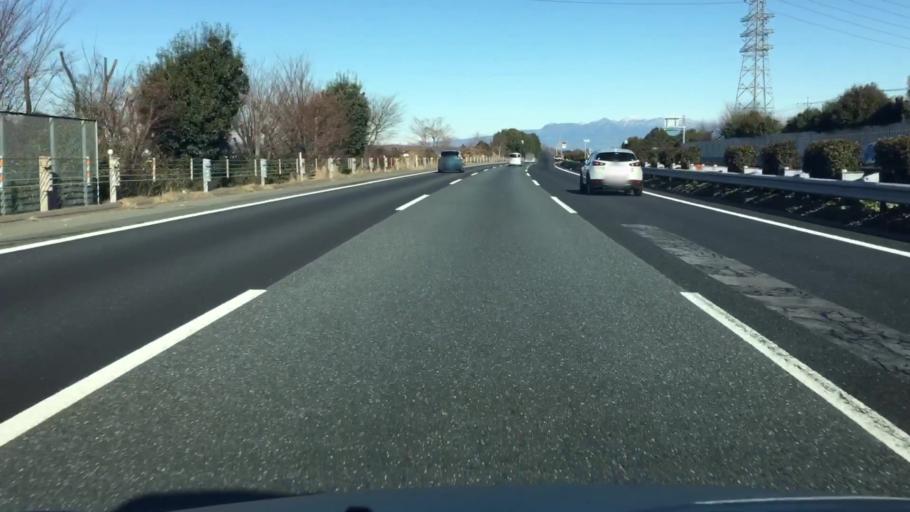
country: JP
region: Saitama
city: Honjo
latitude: 36.1791
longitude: 139.1911
